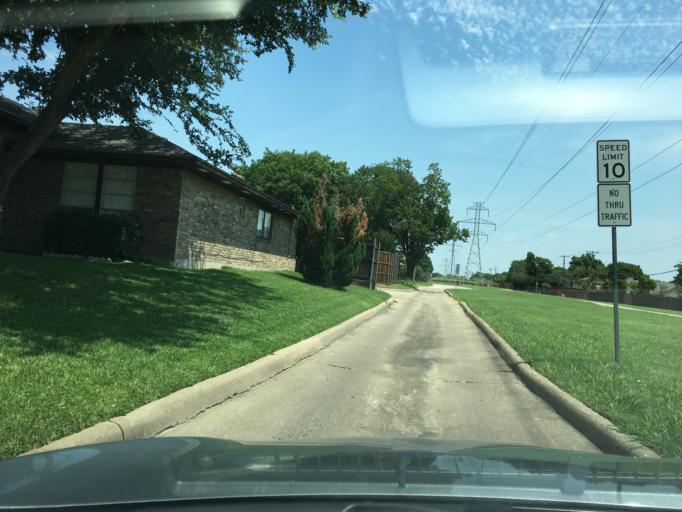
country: US
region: Texas
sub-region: Dallas County
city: Richardson
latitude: 32.9645
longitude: -96.6955
